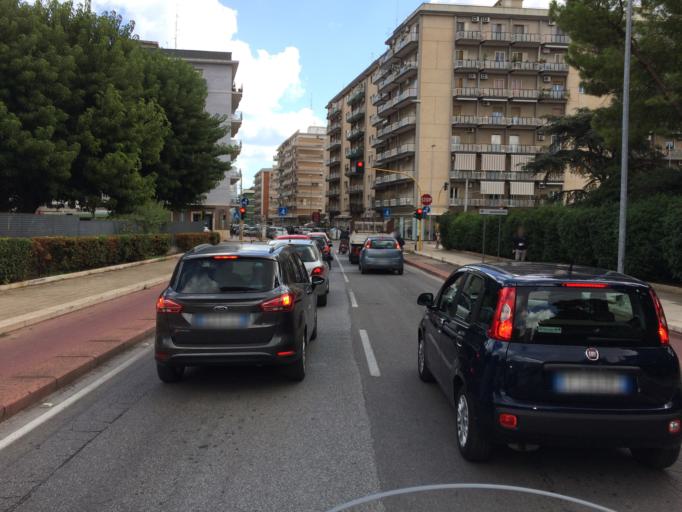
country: IT
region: Apulia
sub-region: Provincia di Bari
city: Bari
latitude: 41.1039
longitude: 16.8746
